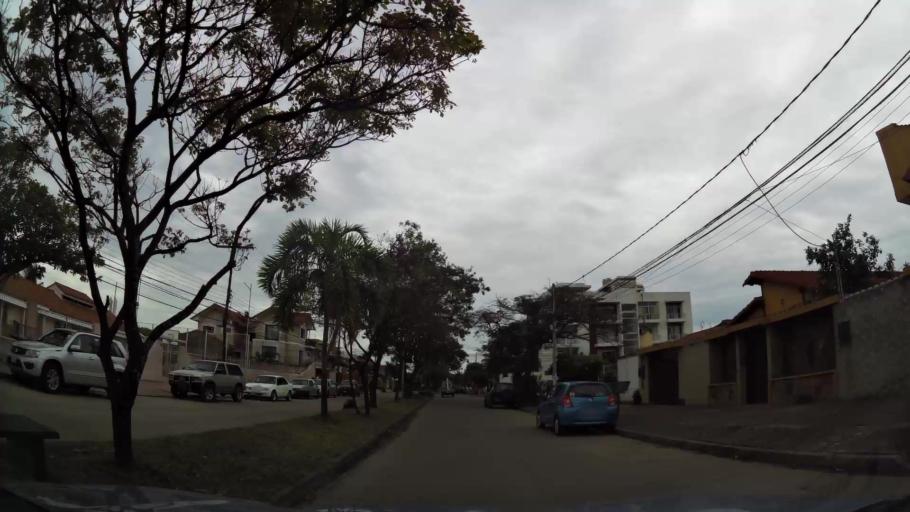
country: BO
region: Santa Cruz
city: Santa Cruz de la Sierra
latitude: -17.7789
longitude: -63.1593
